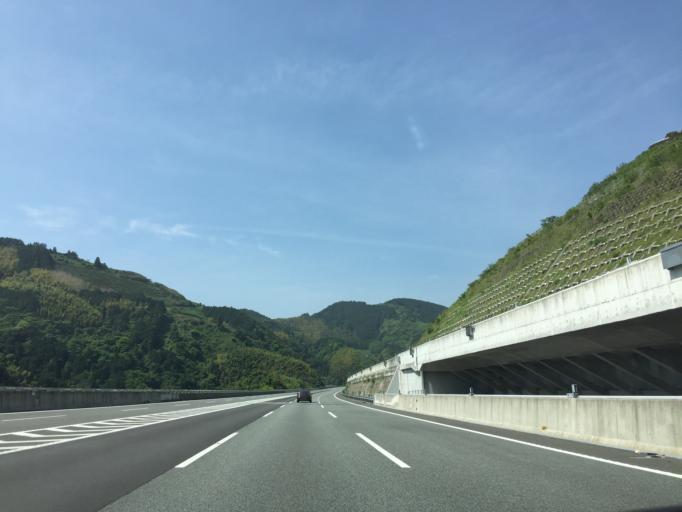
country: JP
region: Shizuoka
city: Shizuoka-shi
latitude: 35.0724
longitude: 138.4585
